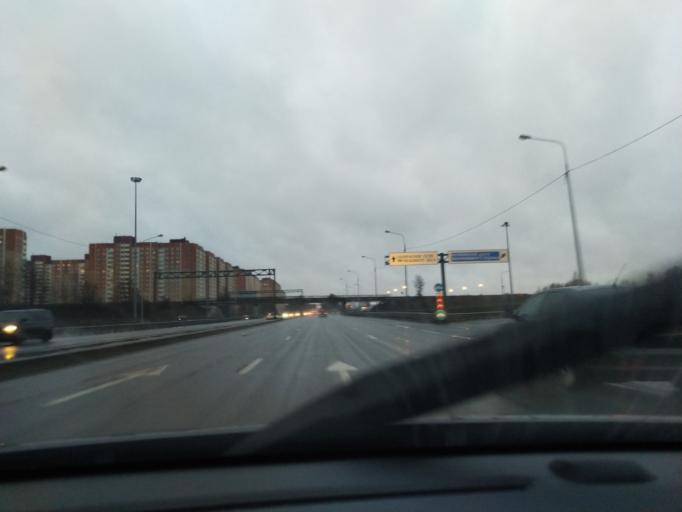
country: RU
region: St.-Petersburg
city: Sosnovaya Polyana
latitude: 59.7987
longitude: 30.1551
